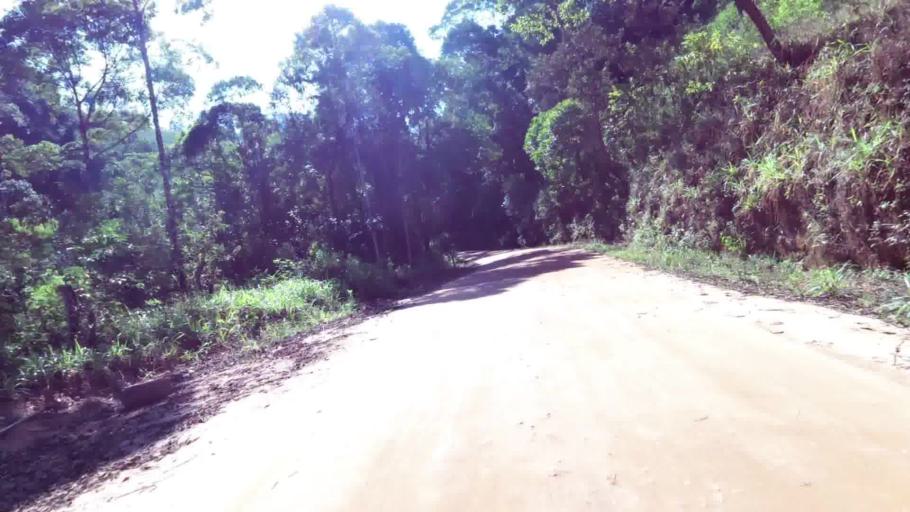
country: BR
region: Espirito Santo
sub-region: Alfredo Chaves
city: Alfredo Chaves
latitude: -20.5778
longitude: -40.7915
